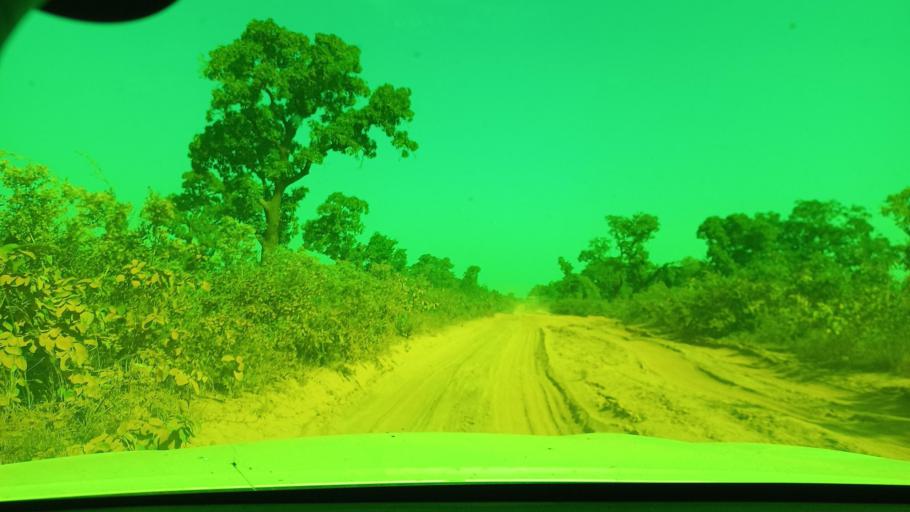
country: ML
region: Bamako
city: Bamako
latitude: 12.3968
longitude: -7.9854
